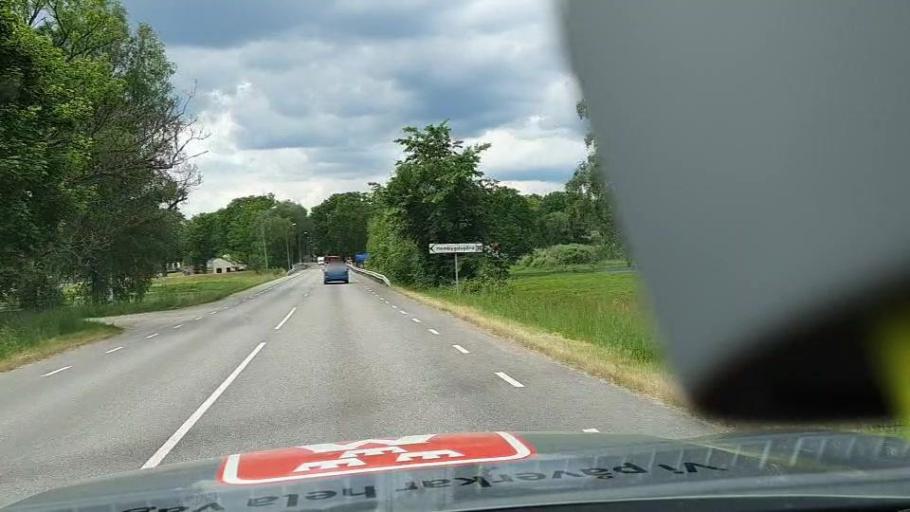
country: SE
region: Kalmar
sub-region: Emmaboda Kommun
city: Emmaboda
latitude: 56.5346
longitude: 15.6037
